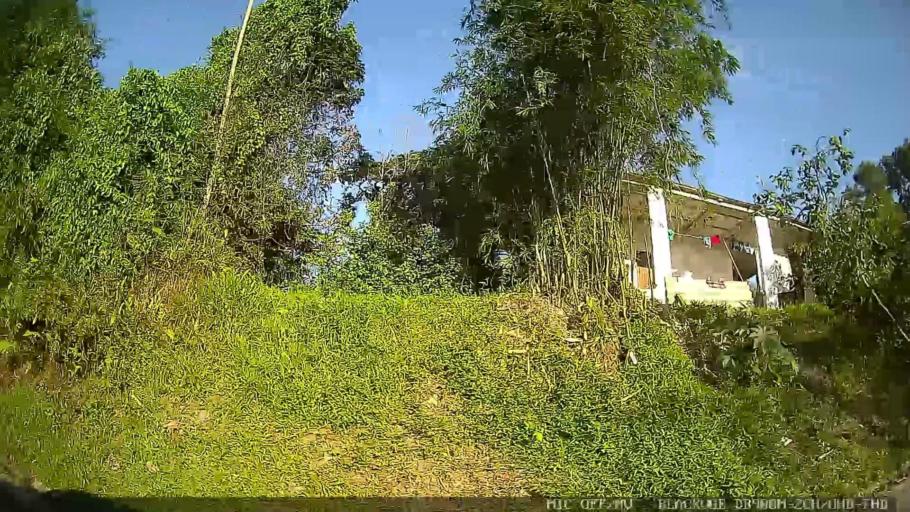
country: BR
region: Sao Paulo
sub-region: Itanhaem
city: Itanhaem
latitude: -24.1506
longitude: -46.8201
